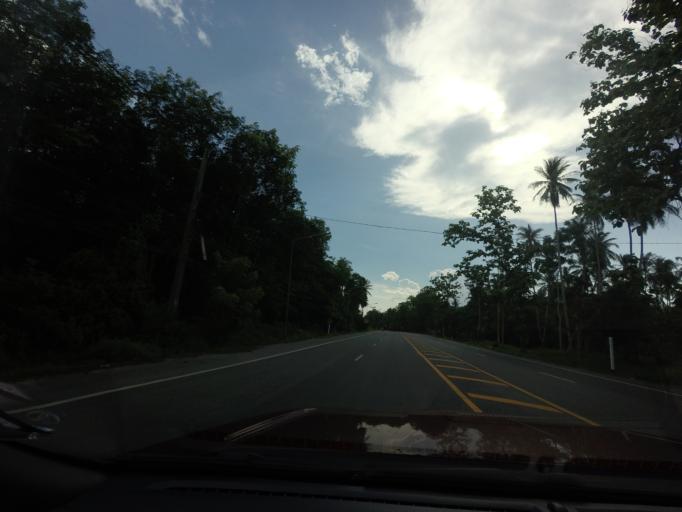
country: TH
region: Pattani
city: Khok Pho
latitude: 6.6770
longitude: 101.1372
